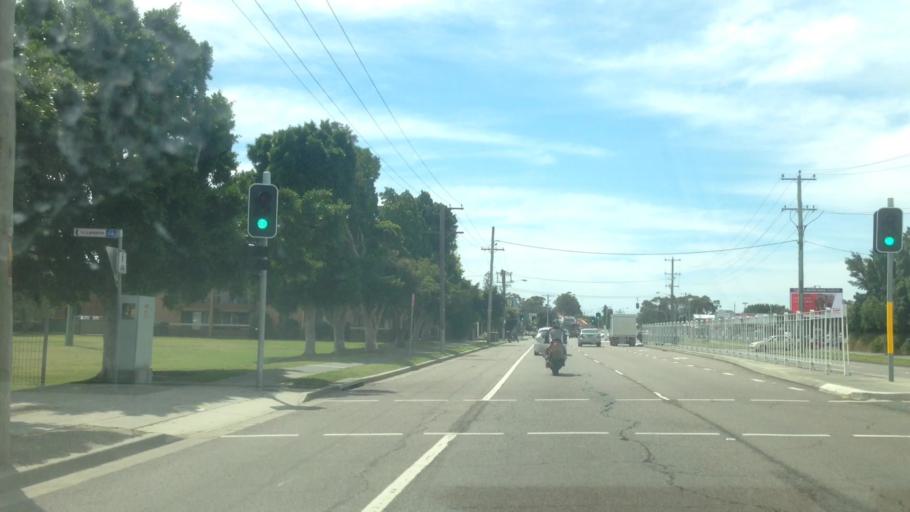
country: AU
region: New South Wales
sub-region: Newcastle
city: Broadmeadow
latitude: -32.9197
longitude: 151.7240
